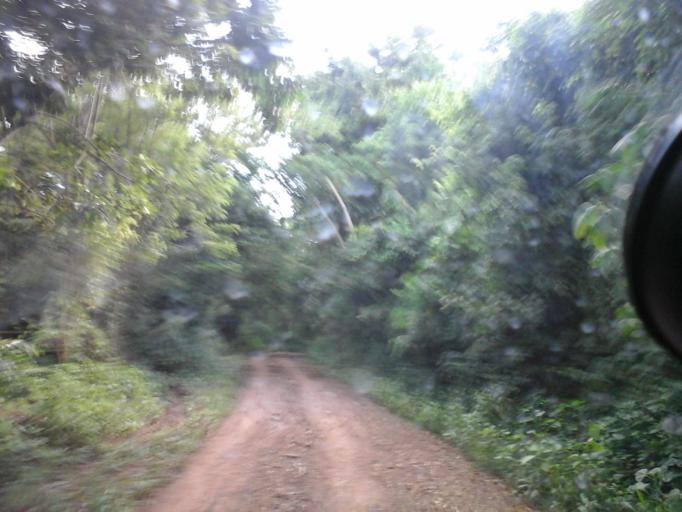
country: CO
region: Cesar
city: San Diego
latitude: 10.2649
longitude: -73.1033
